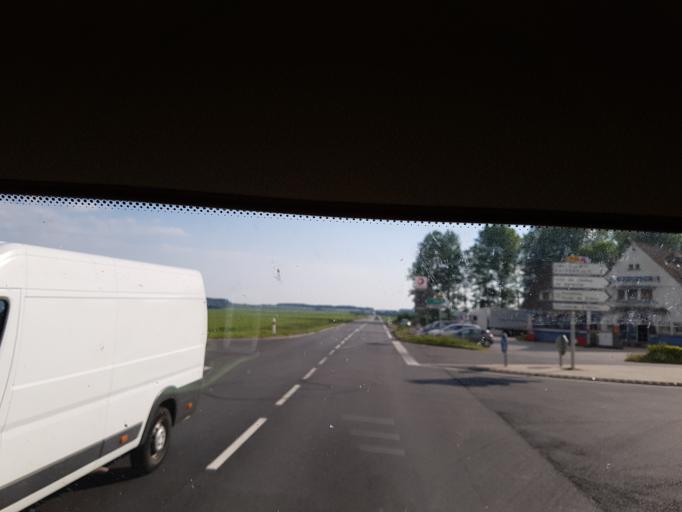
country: FR
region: Picardie
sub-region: Departement de la Somme
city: Crecy-en-Ponthieu
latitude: 50.2430
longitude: 1.9539
